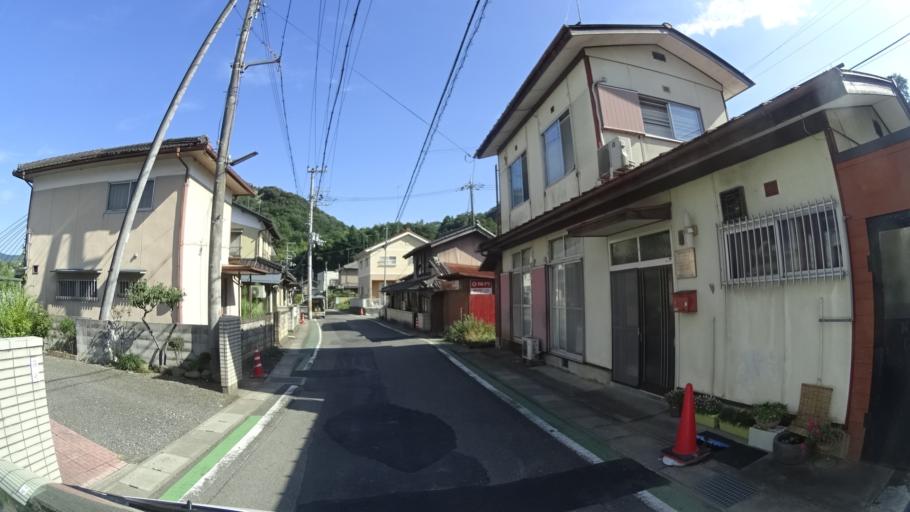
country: JP
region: Kyoto
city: Ayabe
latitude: 35.2918
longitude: 135.2638
